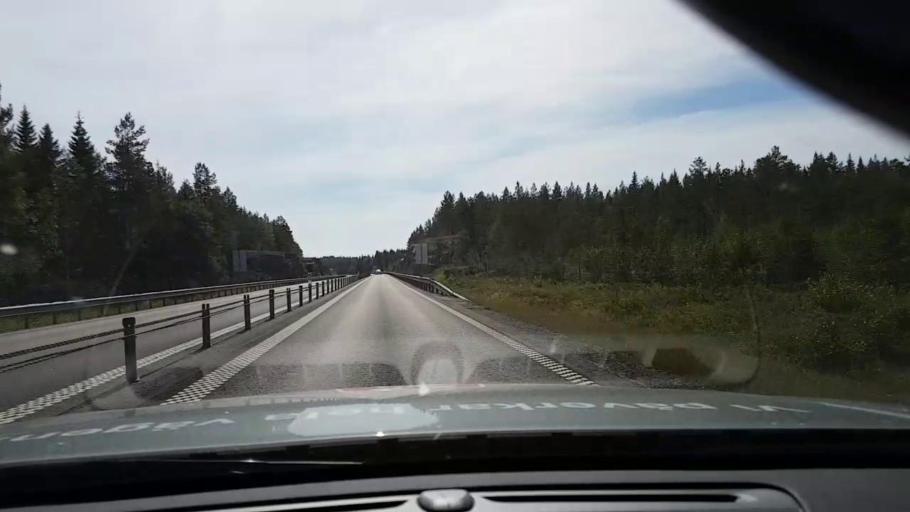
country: SE
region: Vaesternorrland
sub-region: OErnskoeldsviks Kommun
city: Husum
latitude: 63.3977
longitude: 19.1980
